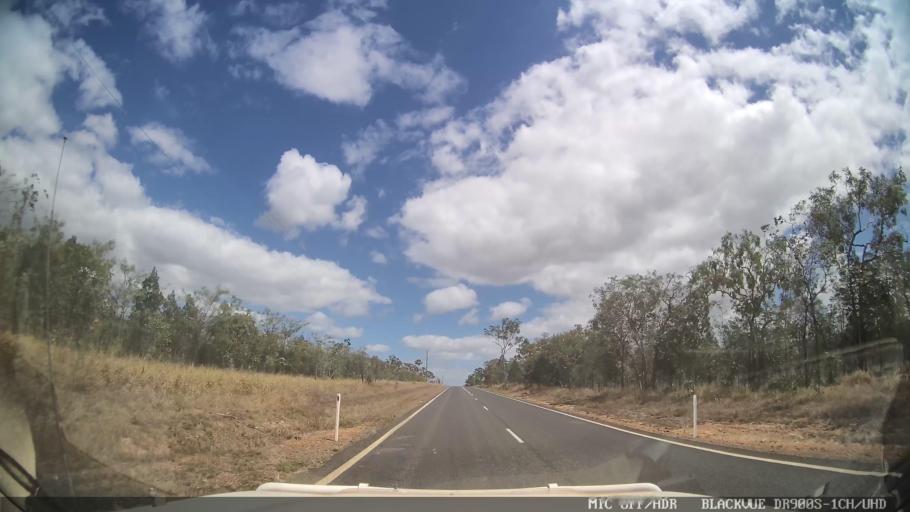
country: AU
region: Queensland
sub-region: Tablelands
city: Ravenshoe
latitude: -17.7290
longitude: 145.0456
